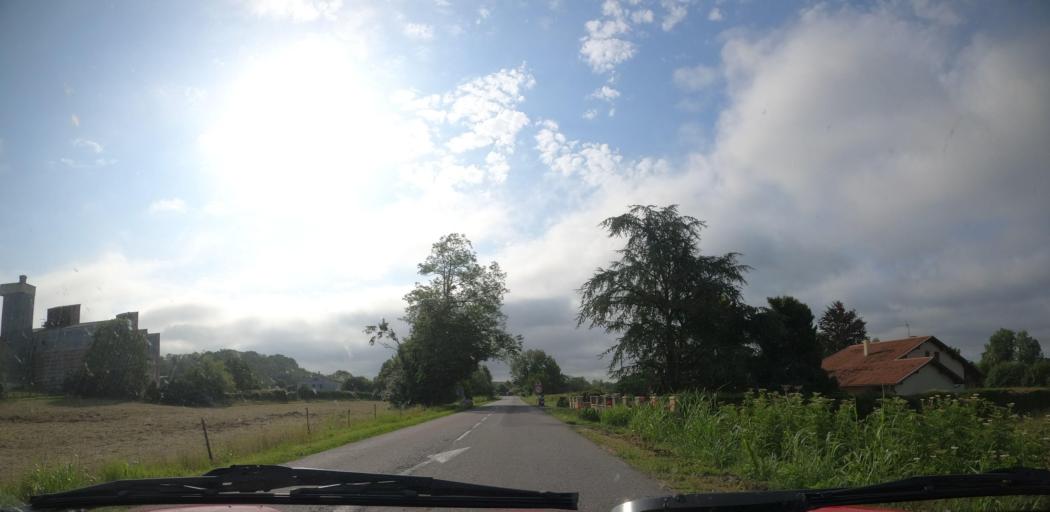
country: FR
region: Aquitaine
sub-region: Departement des Landes
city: Peyrehorade
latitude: 43.5343
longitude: -1.0693
